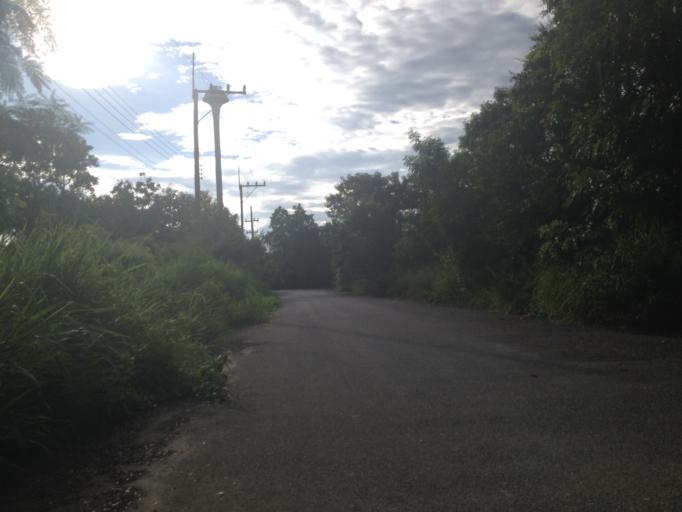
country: TH
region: Chiang Mai
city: Hang Dong
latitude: 18.6796
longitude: 98.8958
